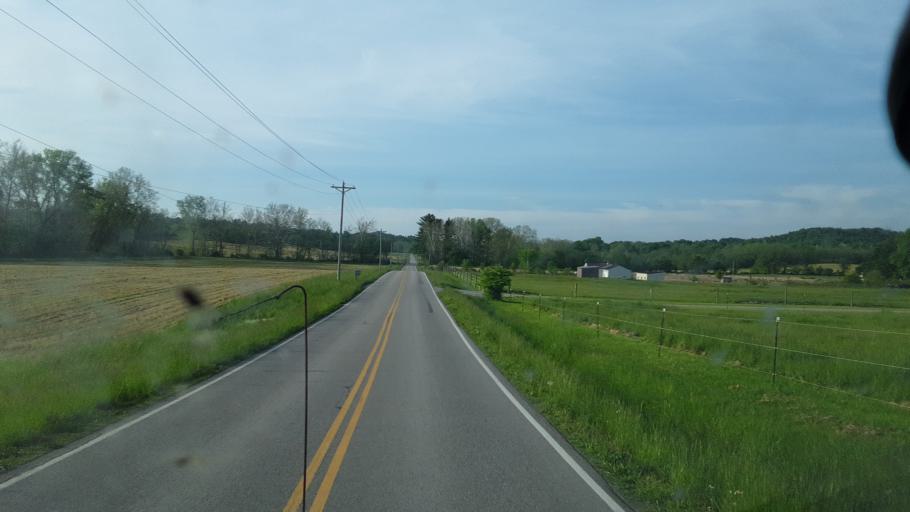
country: US
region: Ohio
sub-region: Ross County
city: Kingston
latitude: 39.4982
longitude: -82.7001
